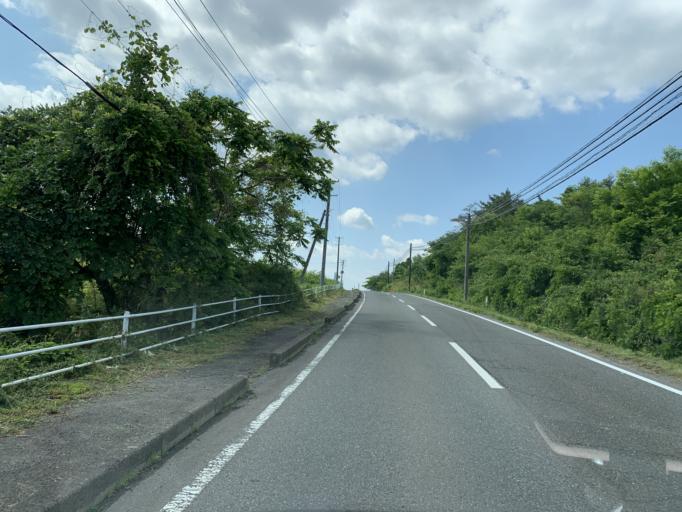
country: JP
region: Miyagi
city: Furukawa
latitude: 38.7619
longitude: 140.9580
